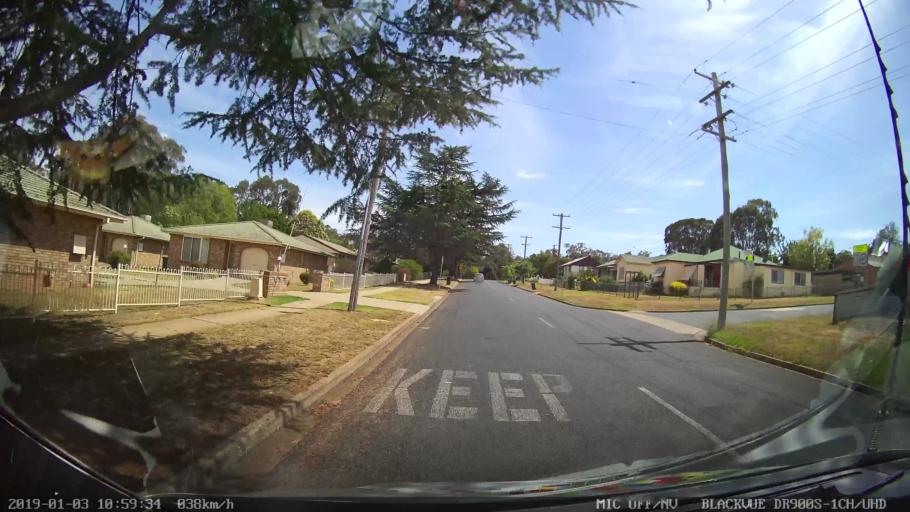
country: AU
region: New South Wales
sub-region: Young
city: Young
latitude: -34.3071
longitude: 148.2991
